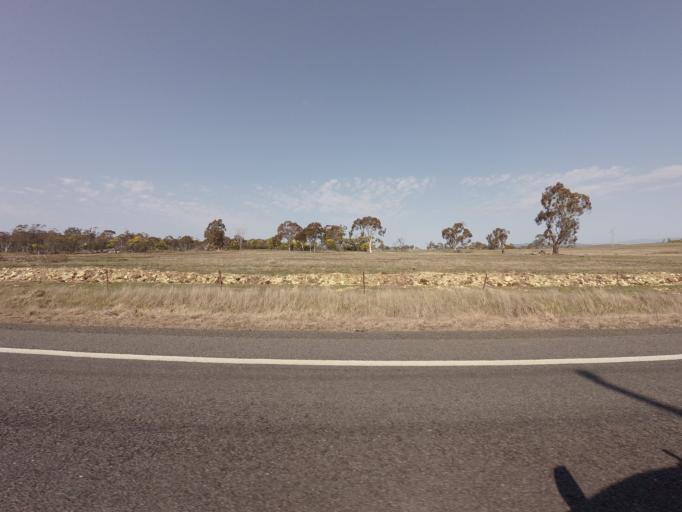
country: AU
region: Tasmania
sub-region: Northern Midlands
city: Evandale
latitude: -41.8347
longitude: 147.4579
